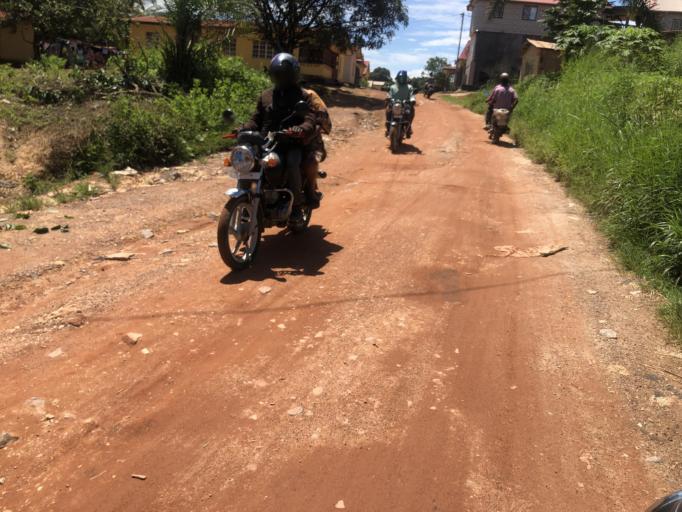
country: SL
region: Eastern Province
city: Koidu
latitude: 8.6424
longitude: -10.9622
